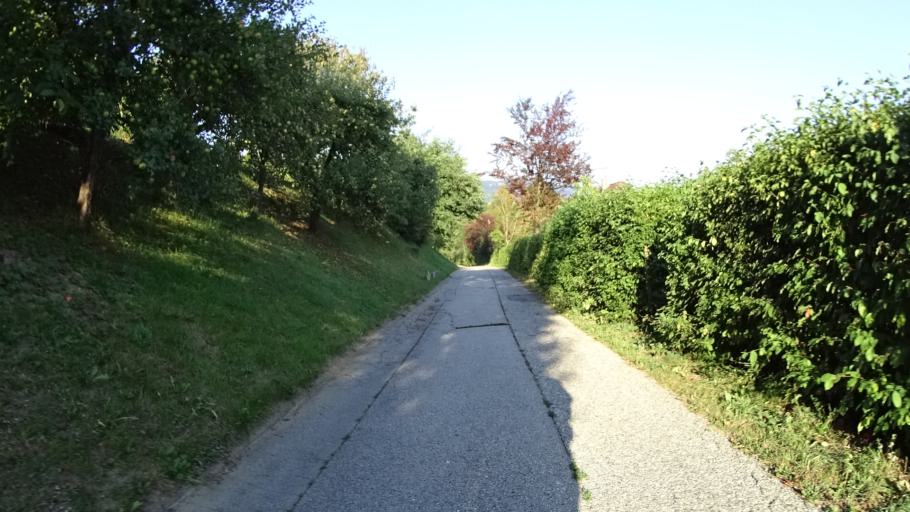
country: AT
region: Carinthia
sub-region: Politischer Bezirk Villach Land
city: Rosegg
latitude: 46.5683
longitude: 14.0326
